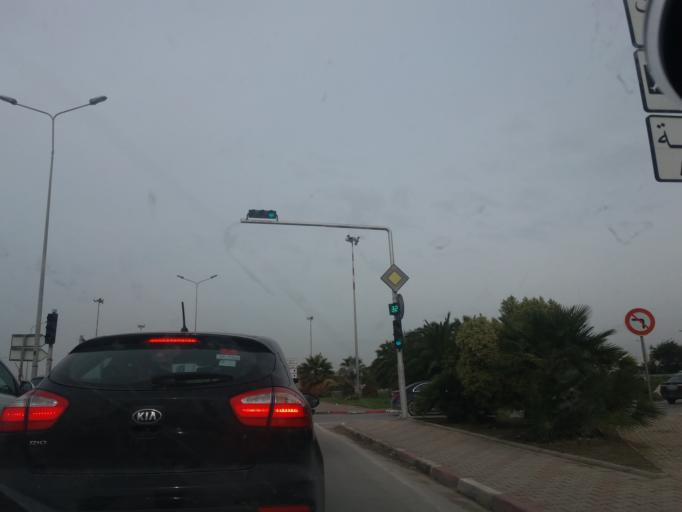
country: TN
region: Tunis
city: Tunis
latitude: 36.8394
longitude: 10.1711
